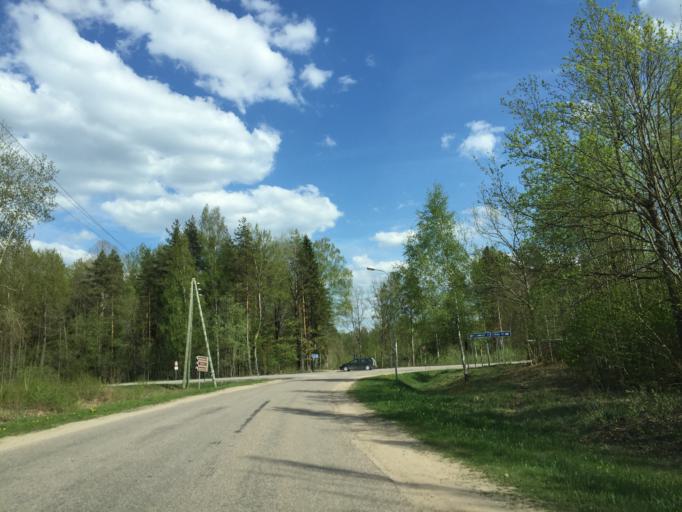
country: LV
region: Limbazu Rajons
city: Limbazi
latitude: 57.4227
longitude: 24.7046
